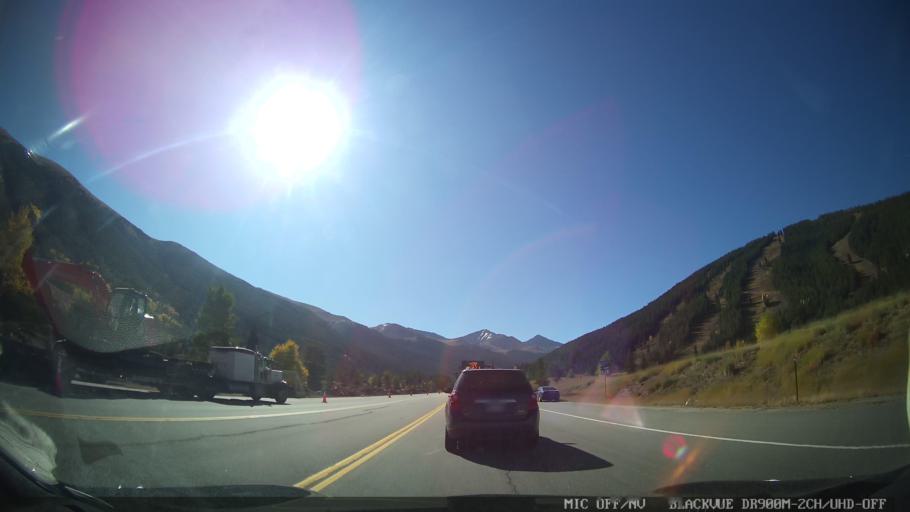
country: US
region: Colorado
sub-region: Summit County
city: Frisco
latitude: 39.4976
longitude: -106.1382
